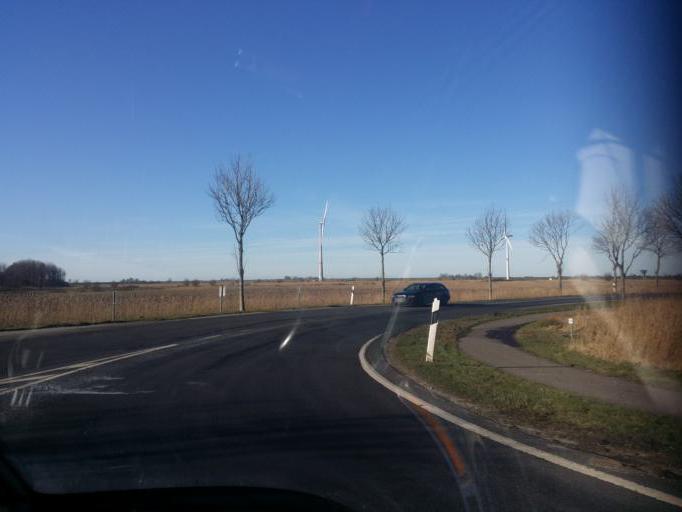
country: DE
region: Schleswig-Holstein
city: Husum
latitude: 54.4516
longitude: 9.0463
